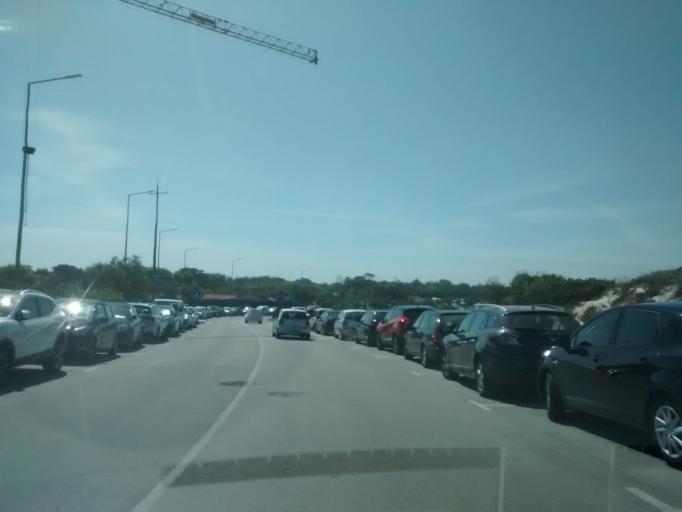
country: PT
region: Coimbra
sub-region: Mira
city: Mira
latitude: 40.4517
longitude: -8.8035
